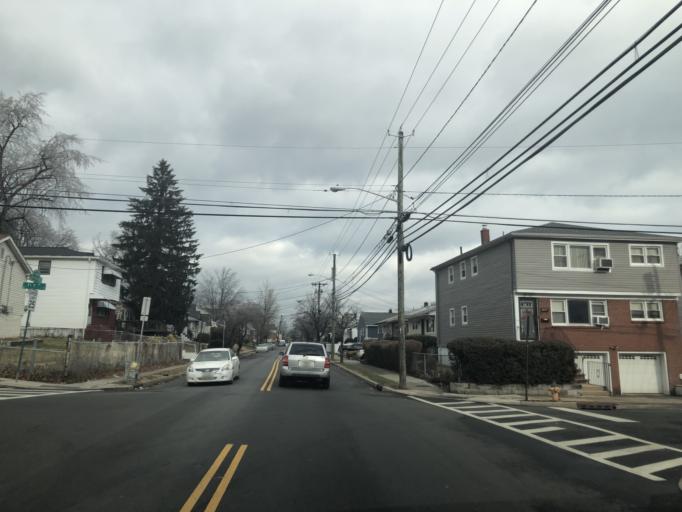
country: US
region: New Jersey
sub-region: Essex County
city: Irvington
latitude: 40.7356
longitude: -74.2334
